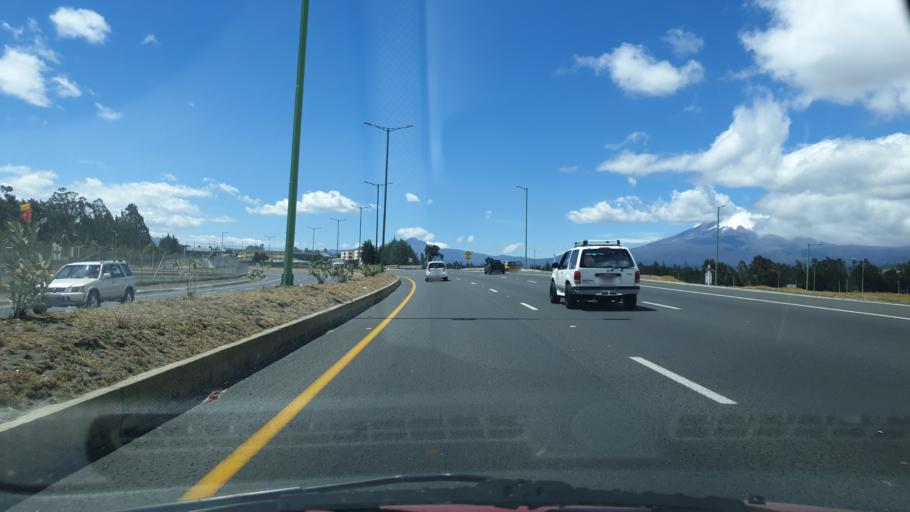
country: EC
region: Cotopaxi
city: Saquisili
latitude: -0.8539
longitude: -78.6201
